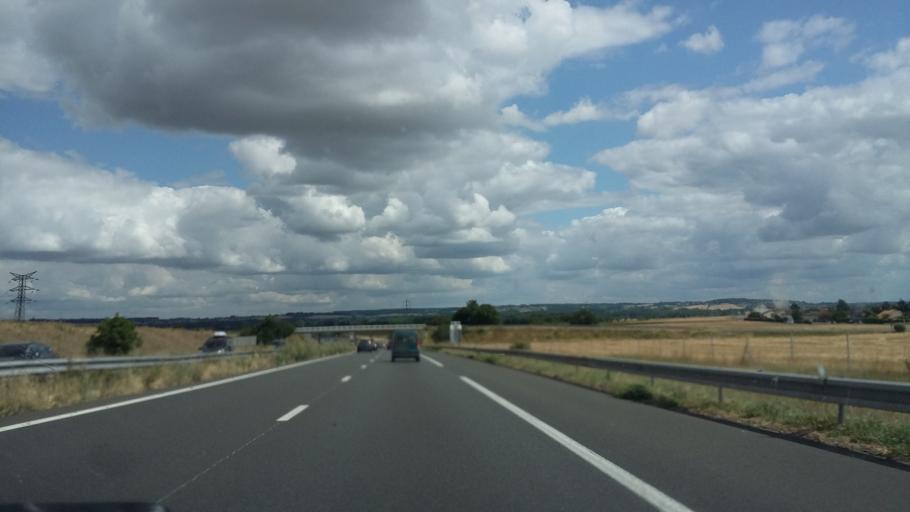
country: FR
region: Poitou-Charentes
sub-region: Departement de la Vienne
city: Jaunay-Clan
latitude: 46.6909
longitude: 0.3662
